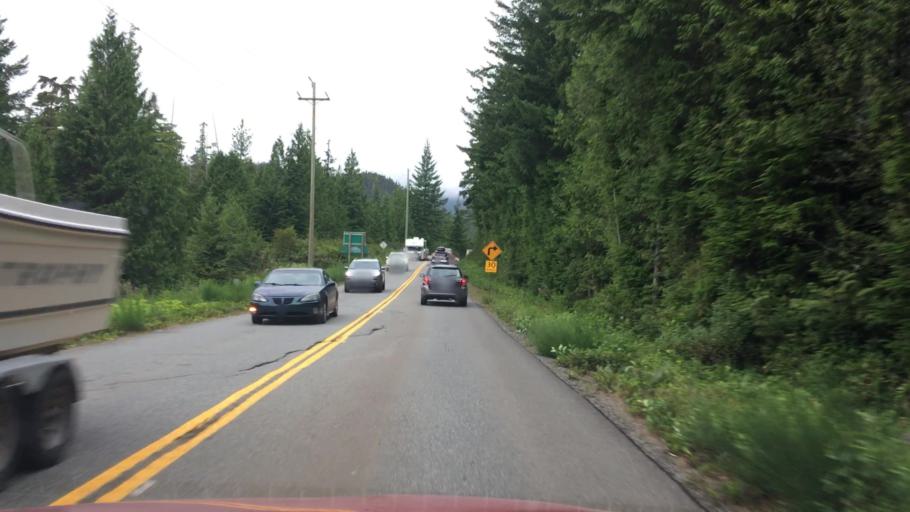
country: CA
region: British Columbia
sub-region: Regional District of Alberni-Clayoquot
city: Ucluelet
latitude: 49.0811
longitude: -125.4650
